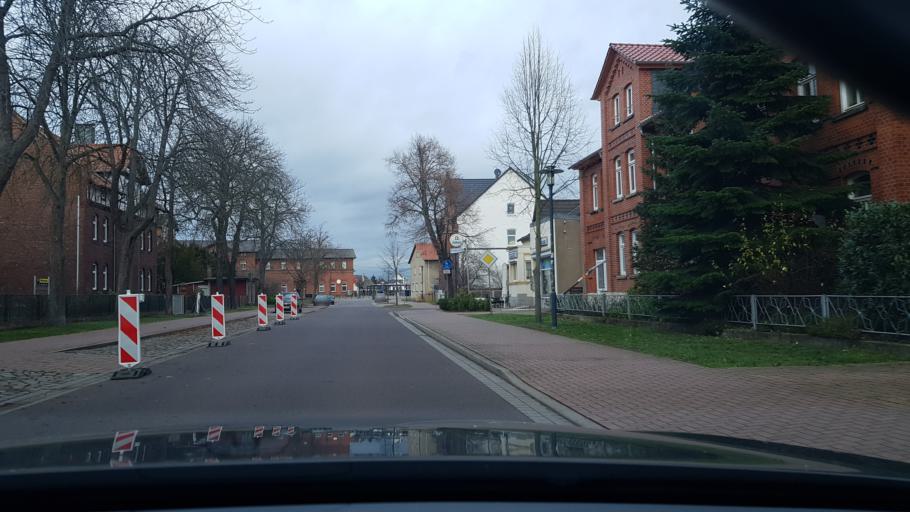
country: DE
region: Saxony-Anhalt
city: Oebisfelde
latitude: 52.4377
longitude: 10.9861
